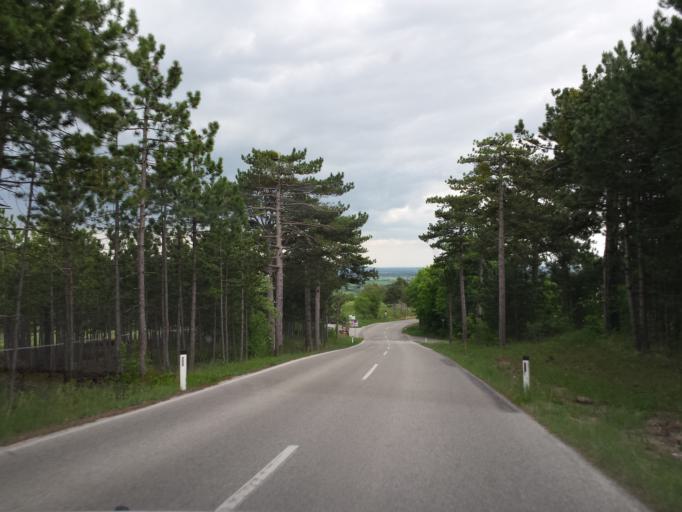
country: AT
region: Lower Austria
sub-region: Politischer Bezirk Baden
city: Hirtenberg
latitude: 47.9128
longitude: 16.1593
